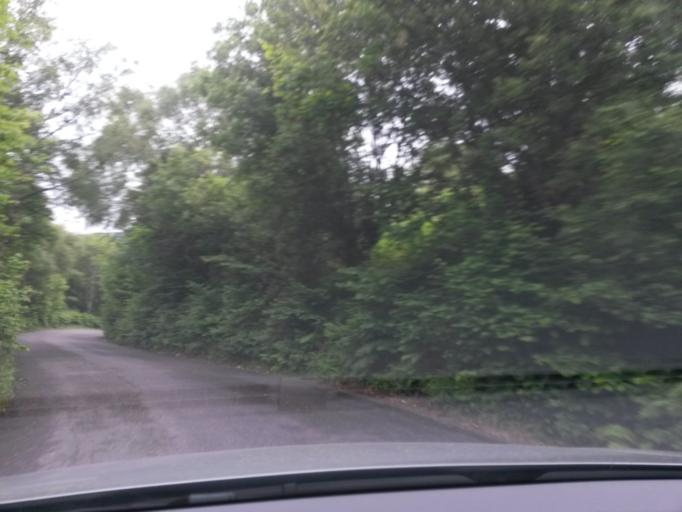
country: IE
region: Munster
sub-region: Ciarrai
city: Killorglin
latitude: 52.0213
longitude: -9.7930
